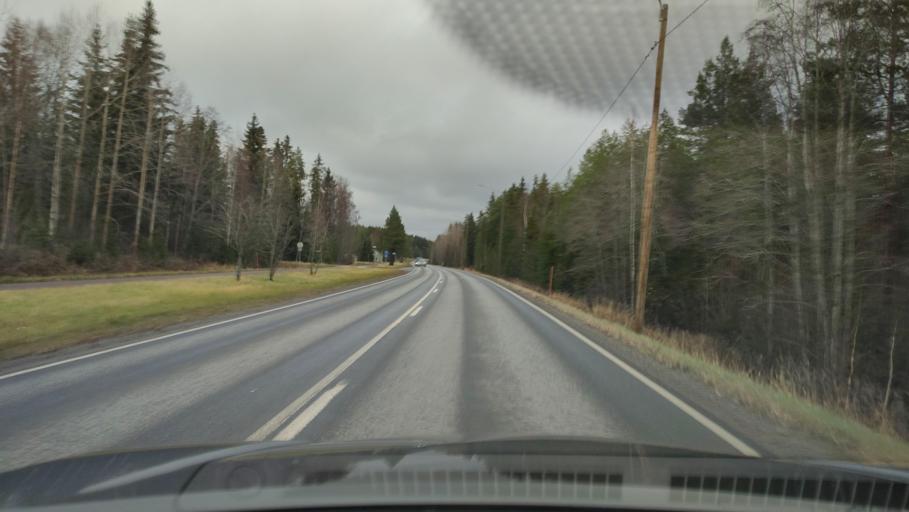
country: FI
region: Southern Ostrobothnia
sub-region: Suupohja
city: Kauhajoki
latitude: 62.3963
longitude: 22.1570
